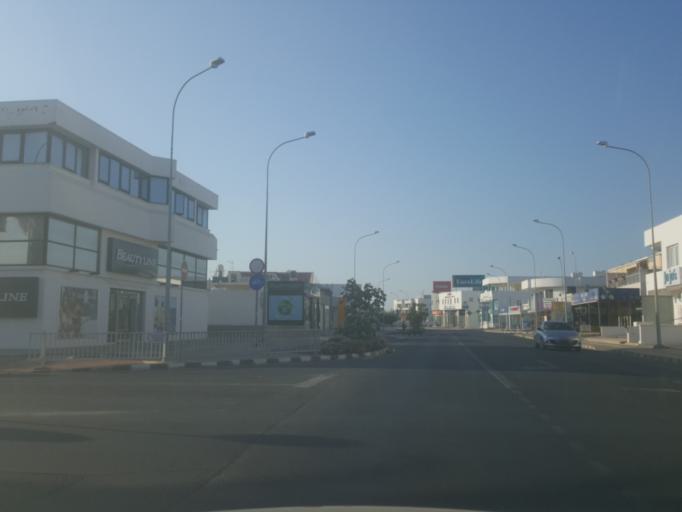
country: CY
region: Ammochostos
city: Paralimni
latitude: 35.0472
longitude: 33.9776
